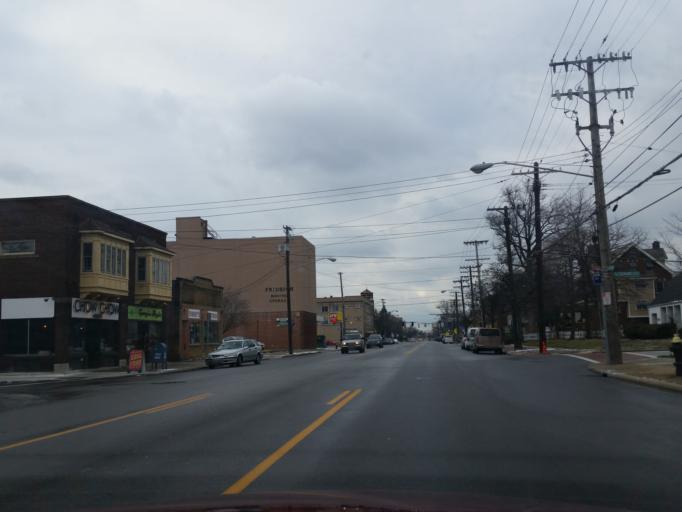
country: US
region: Ohio
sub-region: Cuyahoga County
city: Lakewood
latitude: 41.4771
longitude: -81.7918
